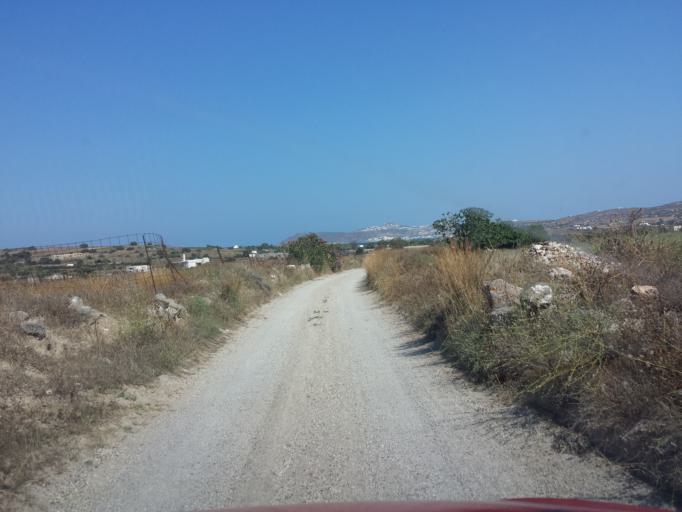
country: GR
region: South Aegean
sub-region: Nomos Kykladon
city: Adamas
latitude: 36.6874
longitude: 24.4888
